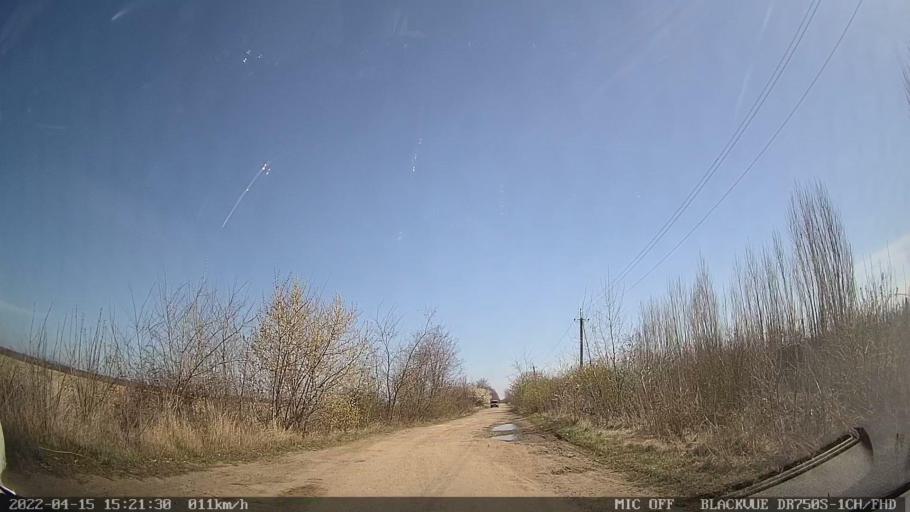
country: MD
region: Raionul Ocnita
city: Otaci
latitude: 48.3836
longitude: 27.9106
